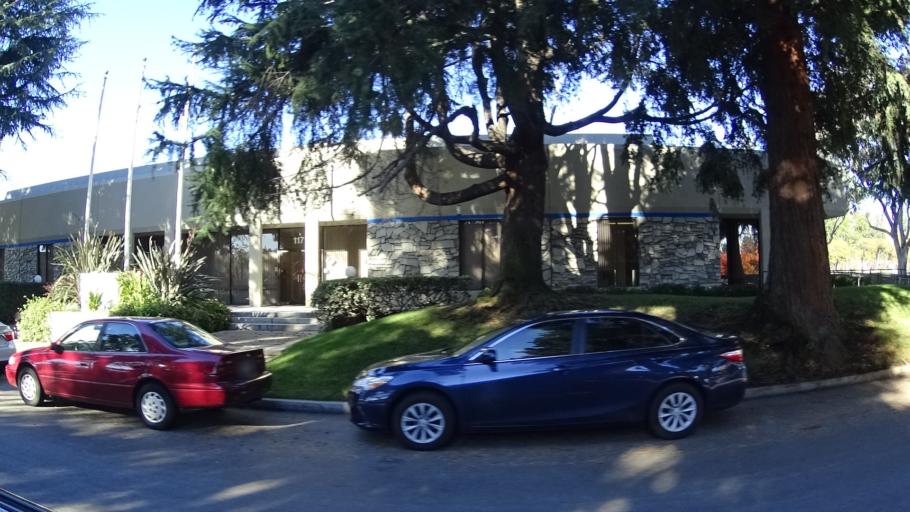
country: US
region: California
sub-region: Santa Clara County
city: Sunnyvale
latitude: 37.3715
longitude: -121.9985
